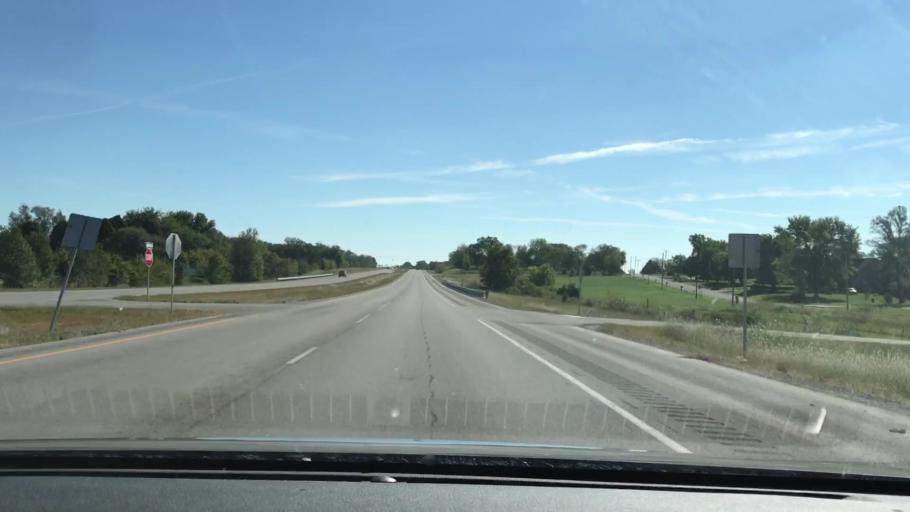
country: US
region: Kentucky
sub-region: Christian County
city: Hopkinsville
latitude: 36.8559
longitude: -87.4192
